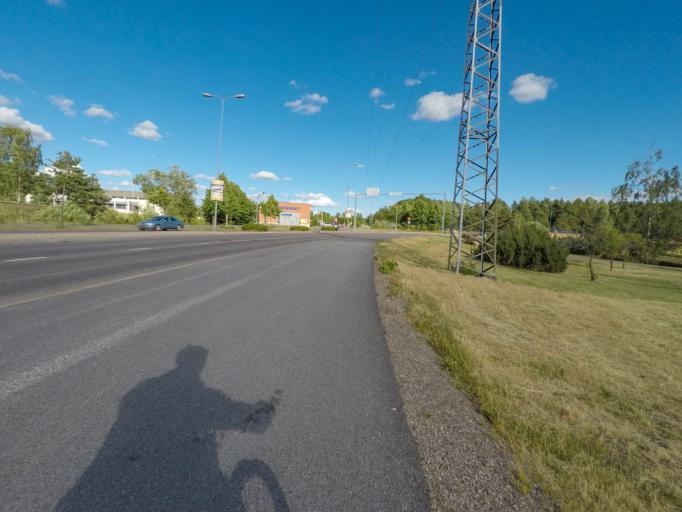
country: FI
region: South Karelia
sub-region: Lappeenranta
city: Lappeenranta
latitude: 61.0647
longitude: 28.1680
